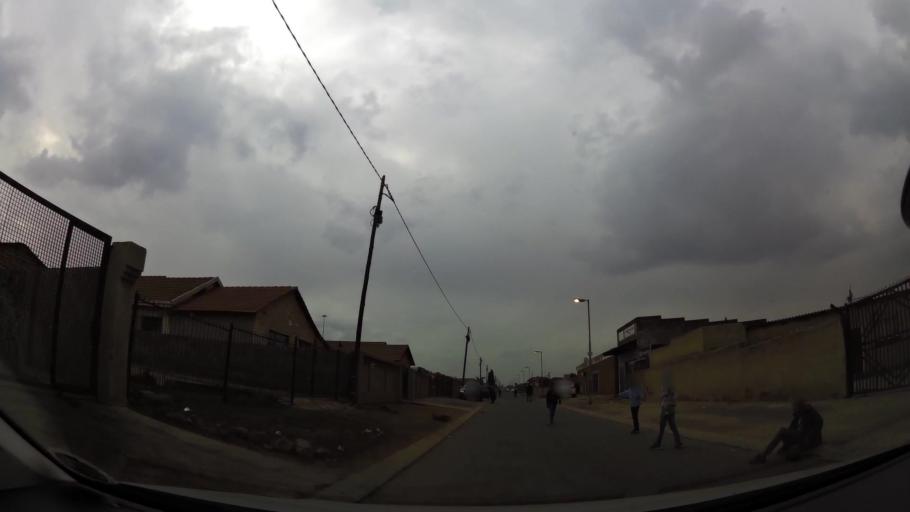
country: ZA
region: Gauteng
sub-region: City of Johannesburg Metropolitan Municipality
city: Soweto
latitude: -26.2639
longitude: 27.8642
